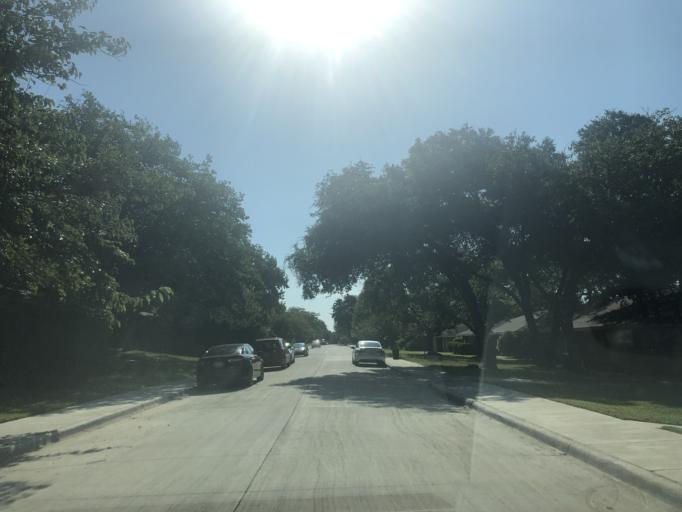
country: US
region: Texas
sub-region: Dallas County
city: Grand Prairie
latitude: 32.7540
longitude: -97.0215
